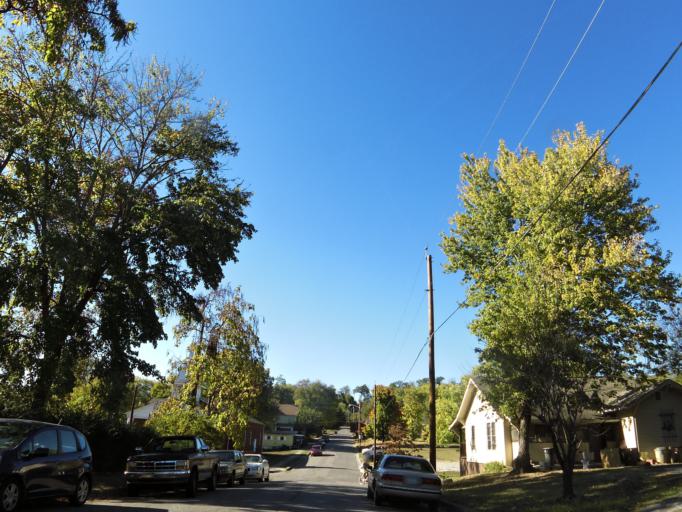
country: US
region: Tennessee
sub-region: Knox County
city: Knoxville
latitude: 35.9852
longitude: -83.9006
